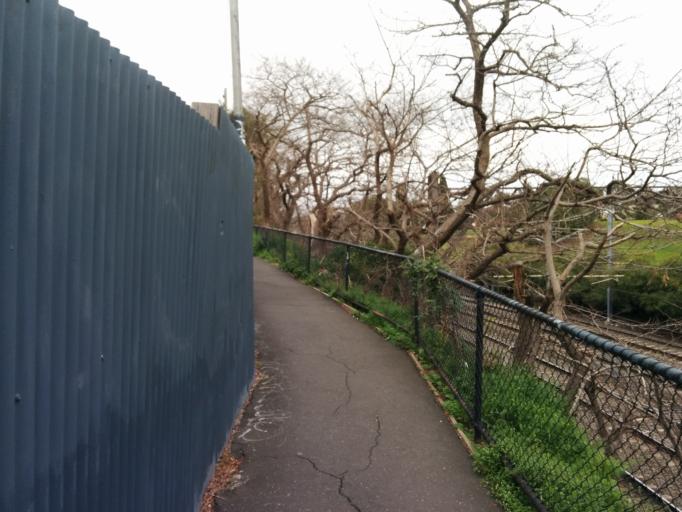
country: AU
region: Victoria
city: Albert Park
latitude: -37.8395
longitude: 144.9925
